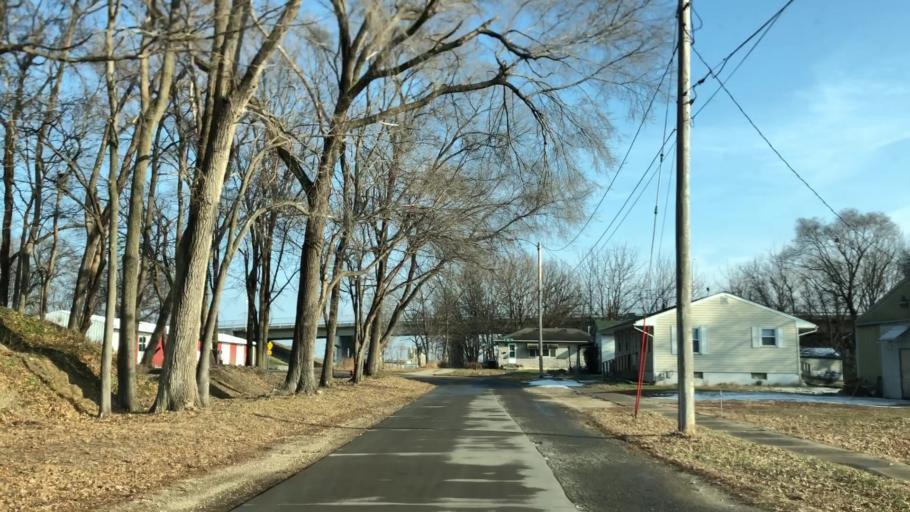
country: US
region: Iowa
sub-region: Marshall County
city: Marshalltown
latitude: 42.0412
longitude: -92.9201
